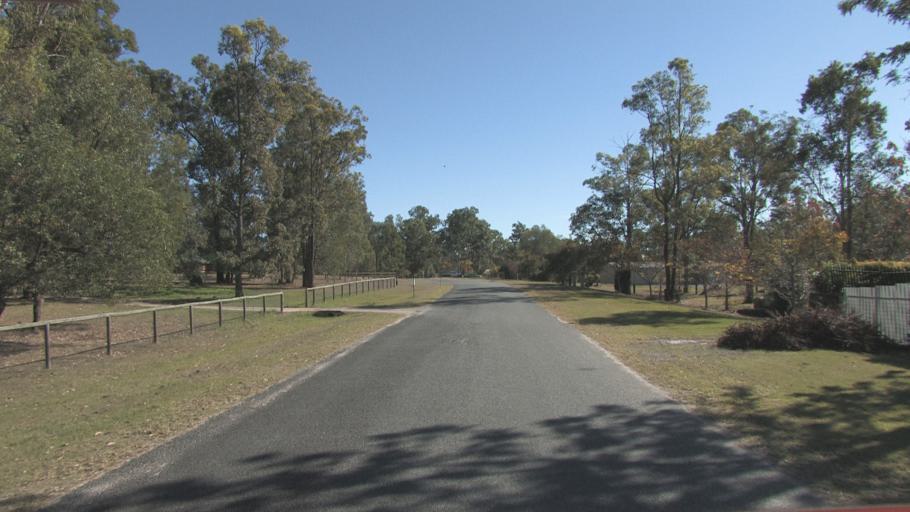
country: AU
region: Queensland
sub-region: Logan
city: North Maclean
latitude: -27.8283
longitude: 152.9395
